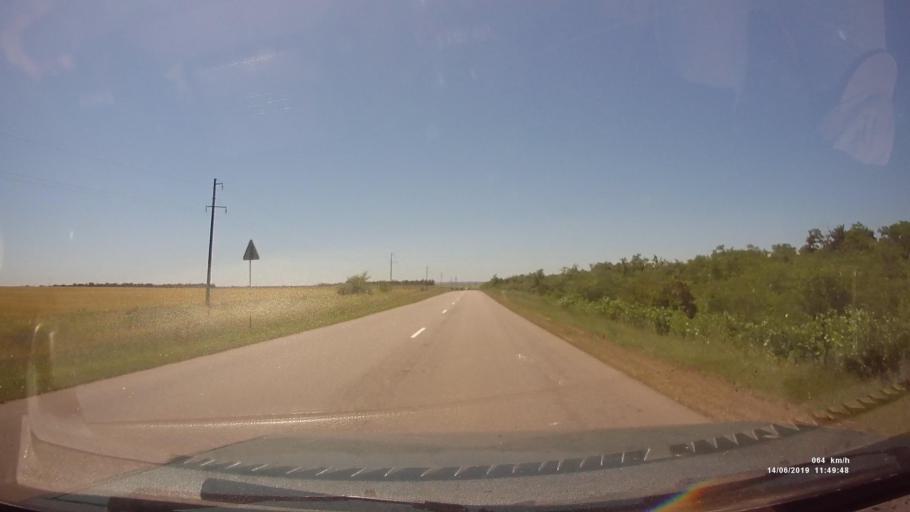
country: RU
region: Rostov
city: Kazanskaya
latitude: 49.8518
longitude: 41.2735
